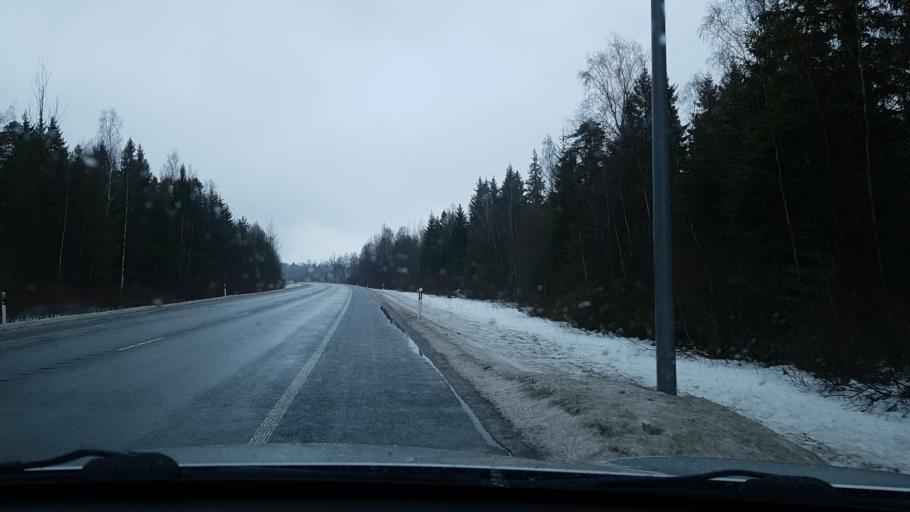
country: EE
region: Raplamaa
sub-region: Kohila vald
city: Kohila
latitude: 59.1311
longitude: 24.7918
